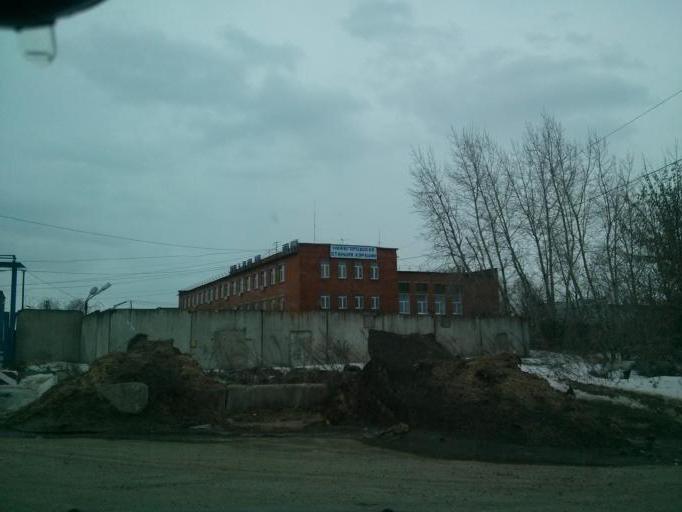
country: RU
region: Nizjnij Novgorod
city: Afonino
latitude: 56.2850
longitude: 44.1196
